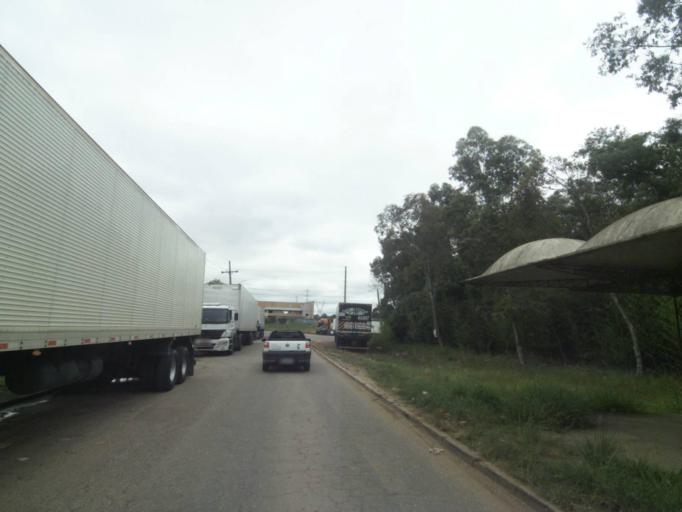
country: BR
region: Parana
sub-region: Araucaria
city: Araucaria
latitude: -25.5427
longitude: -49.3152
